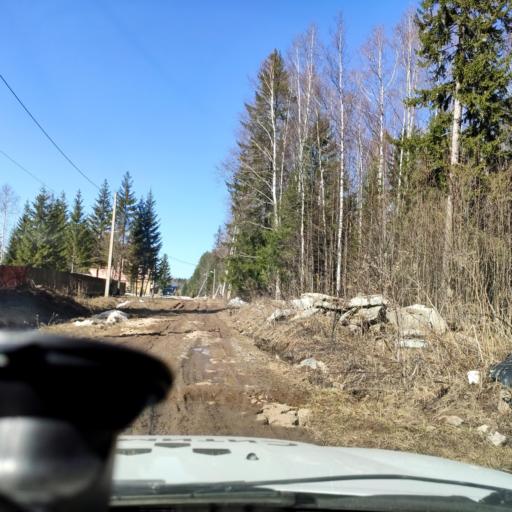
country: RU
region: Perm
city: Ferma
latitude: 57.9274
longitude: 56.4255
